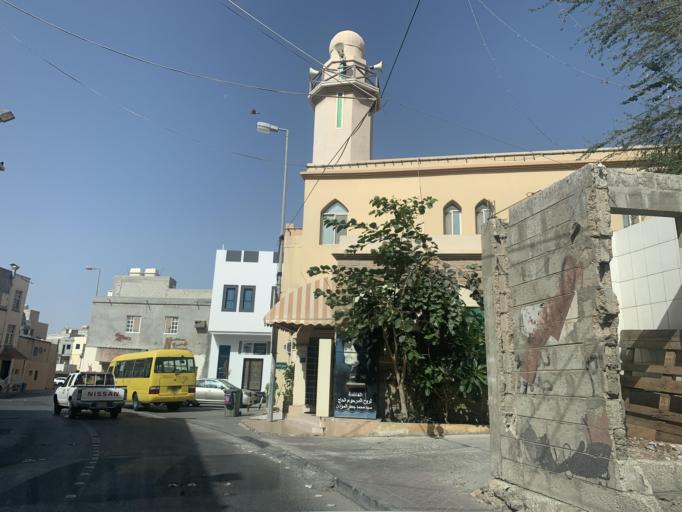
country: BH
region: Manama
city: Jidd Hafs
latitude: 26.2097
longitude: 50.5567
